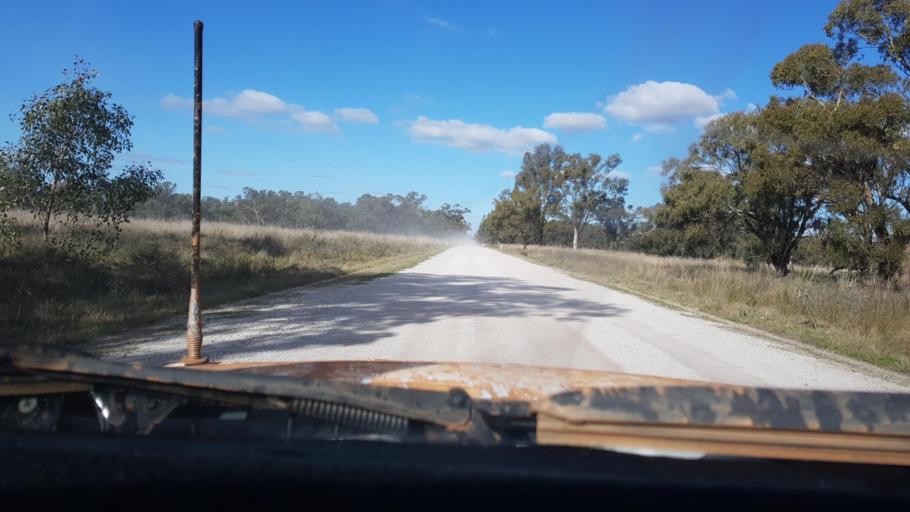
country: AU
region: New South Wales
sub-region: Lachlan
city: Condobolin
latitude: -33.1269
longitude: 147.2549
